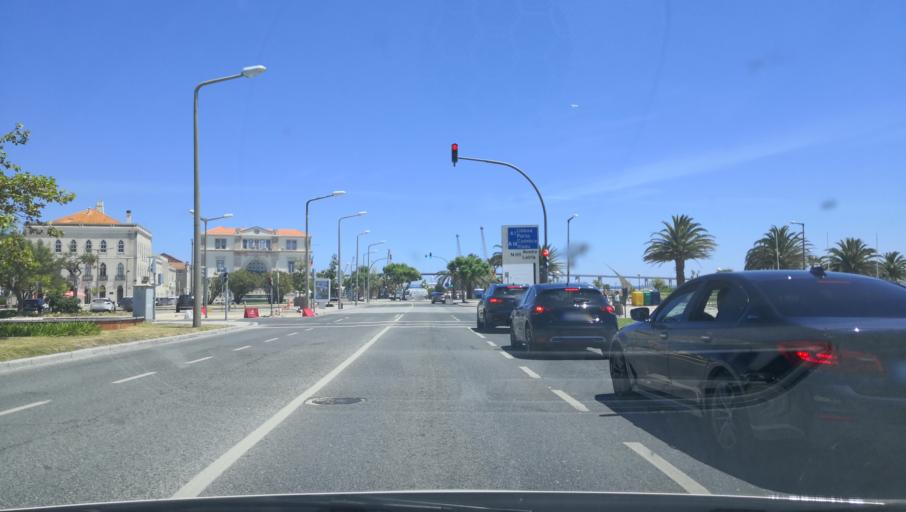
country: PT
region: Coimbra
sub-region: Figueira da Foz
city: Figueira da Foz
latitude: 40.1483
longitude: -8.8571
